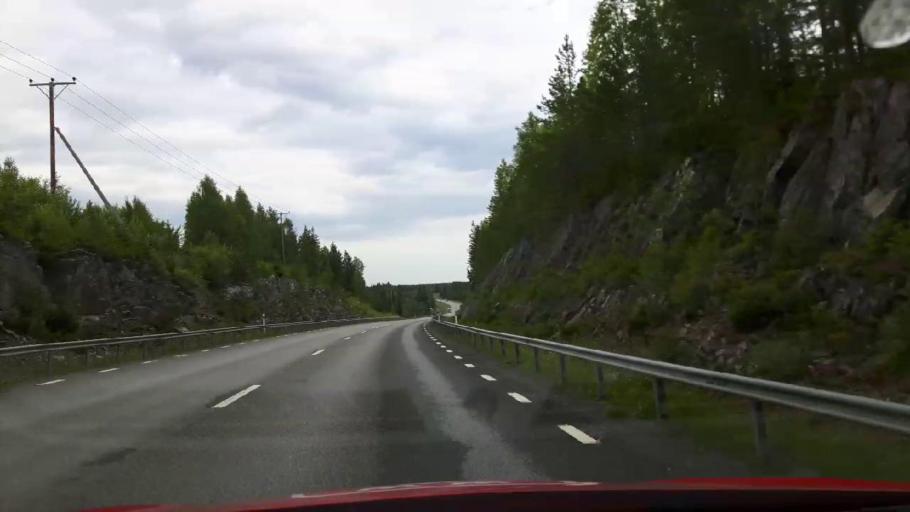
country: SE
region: Jaemtland
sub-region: Stroemsunds Kommun
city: Stroemsund
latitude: 63.6363
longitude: 15.3603
